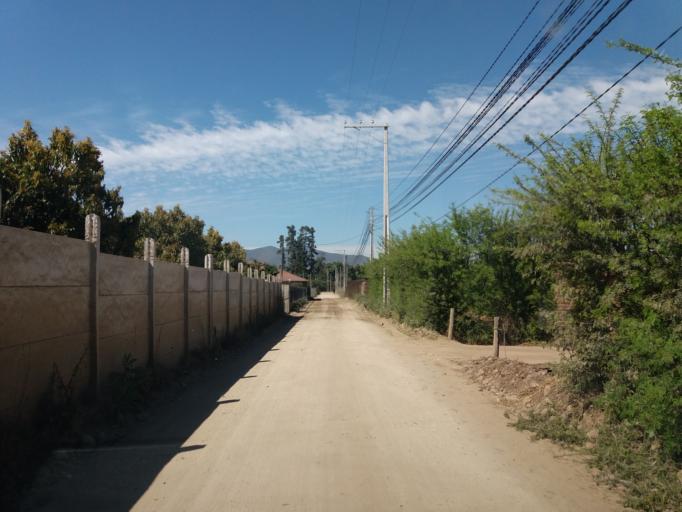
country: CL
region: Valparaiso
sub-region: Provincia de Quillota
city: Quillota
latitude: -32.8729
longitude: -71.2243
